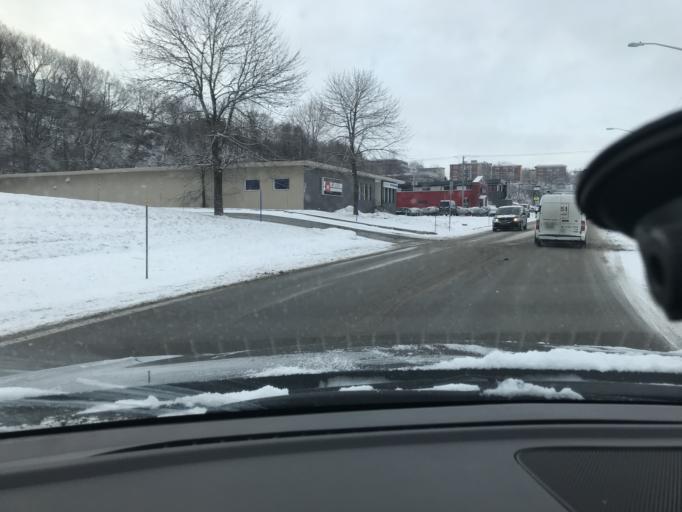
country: CA
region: Quebec
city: Quebec
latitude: 46.7948
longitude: -71.2707
